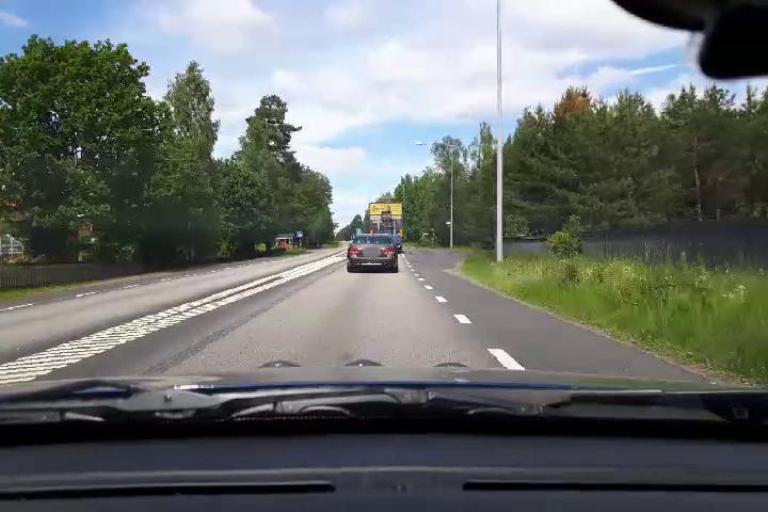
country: SE
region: Uppsala
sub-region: Osthammars Kommun
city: Bjorklinge
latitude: 60.0390
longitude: 17.5505
